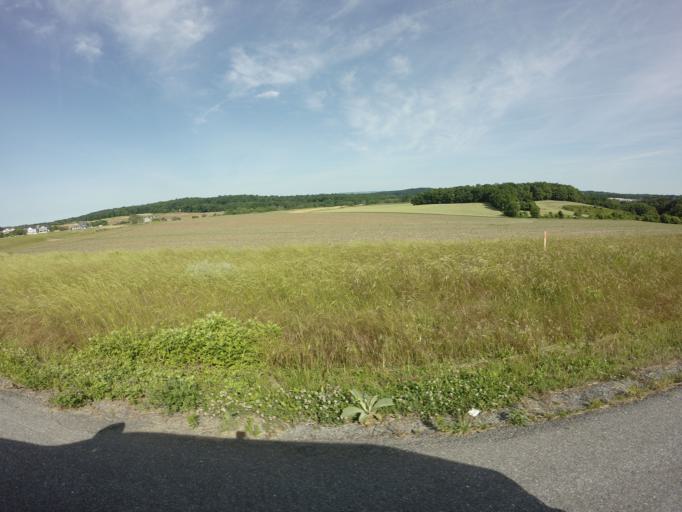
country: US
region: Maryland
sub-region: Frederick County
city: Green Valley
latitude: 39.3599
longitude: -77.2769
